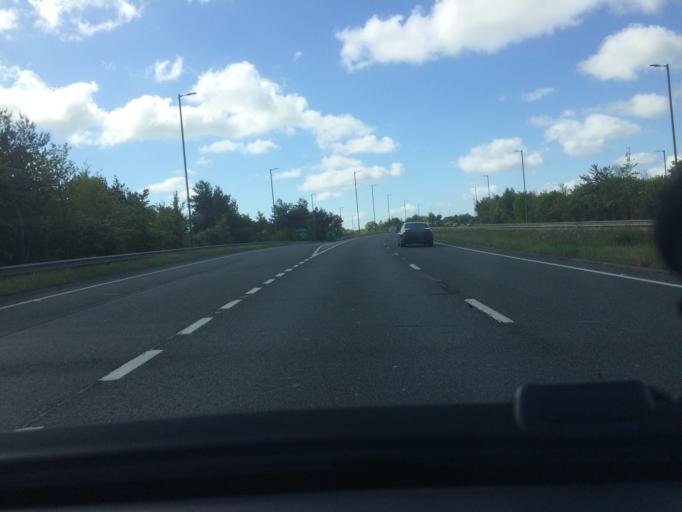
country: GB
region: Wales
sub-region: Wrexham
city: Gresford
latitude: 53.0767
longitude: -2.9863
